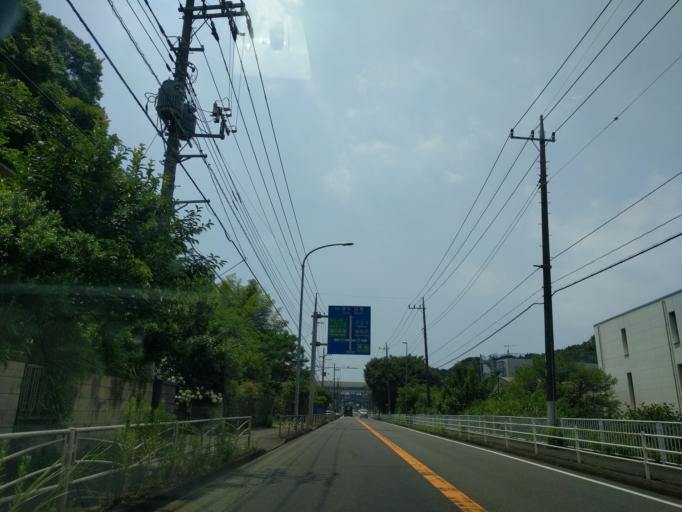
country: JP
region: Kanagawa
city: Minami-rinkan
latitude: 35.4969
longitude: 139.4989
